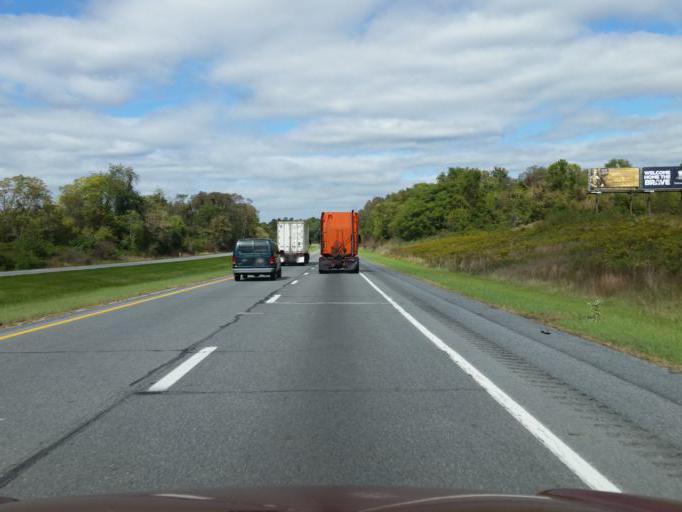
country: US
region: Pennsylvania
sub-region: Dauphin County
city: Middletown
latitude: 40.2160
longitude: -76.7094
